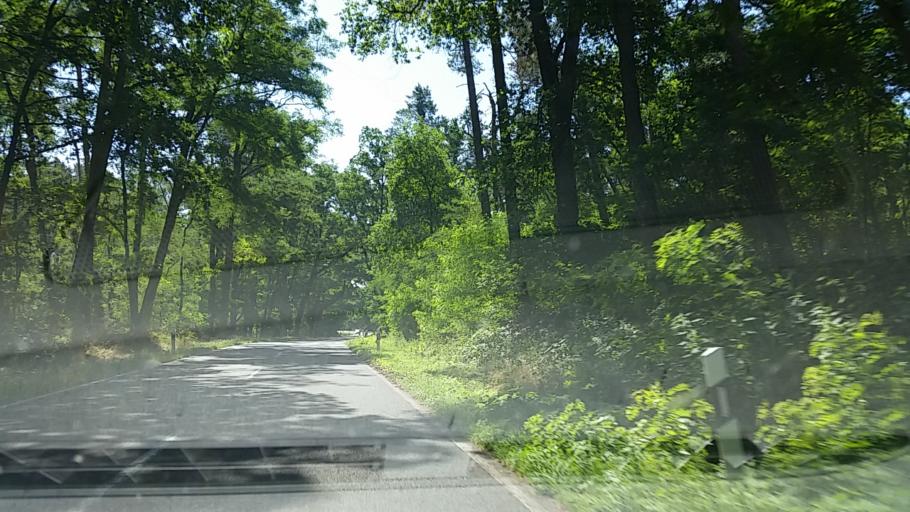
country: DE
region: Saxony-Anhalt
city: Pretzsch
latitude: 51.6831
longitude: 12.8023
